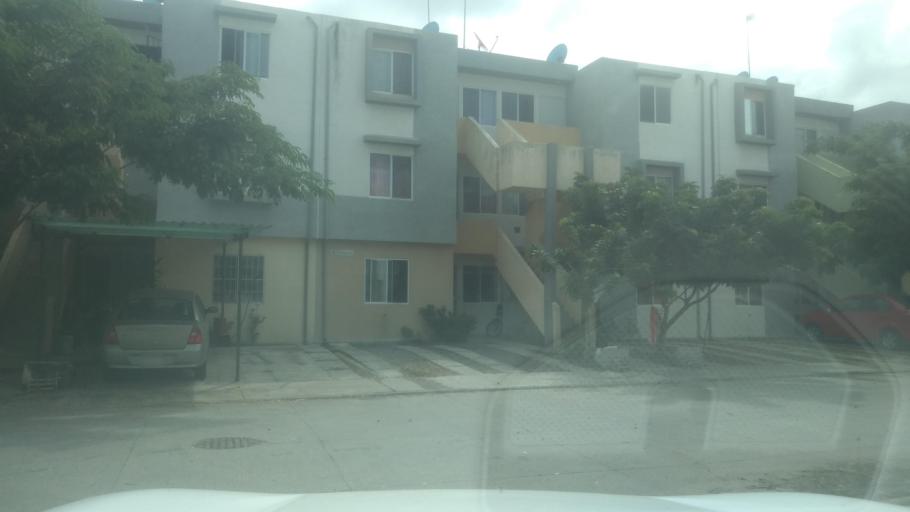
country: MX
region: Veracruz
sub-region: Medellin
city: Fraccionamiento Arboledas San Ramon
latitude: 19.0922
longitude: -96.1669
